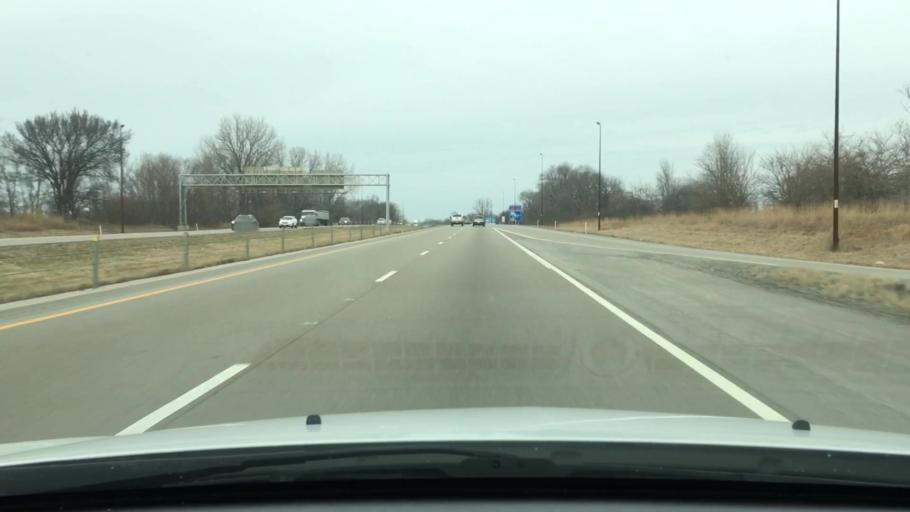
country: US
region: Illinois
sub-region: Sangamon County
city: Grandview
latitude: 39.8046
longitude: -89.5943
